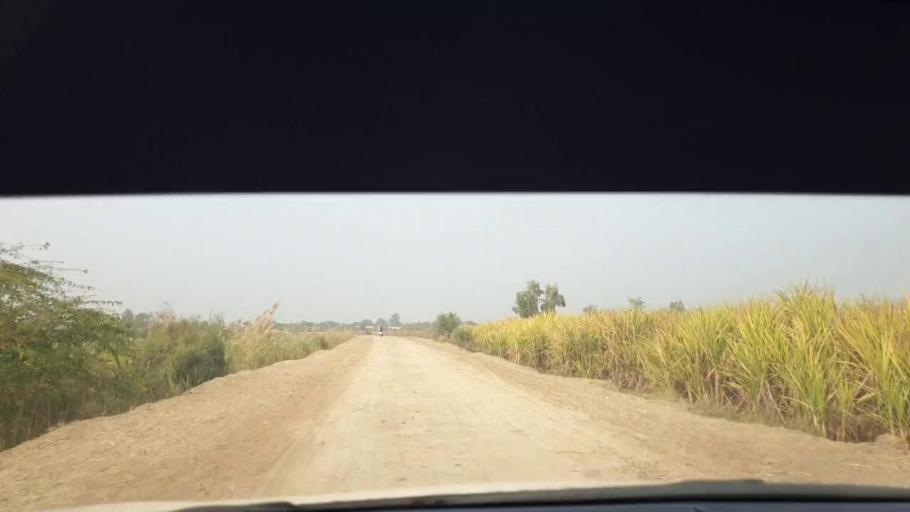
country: PK
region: Sindh
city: Berani
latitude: 25.8197
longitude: 68.8429
